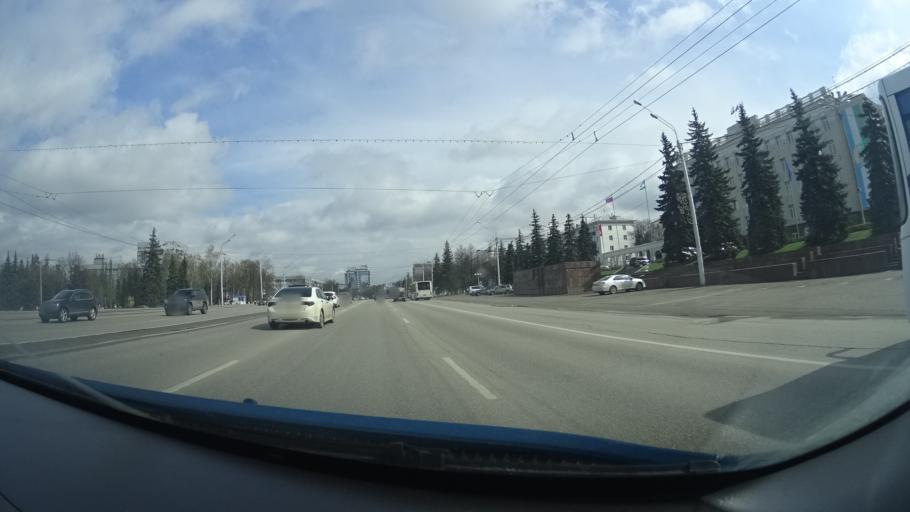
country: RU
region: Bashkortostan
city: Ufa
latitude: 54.7718
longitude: 56.0252
